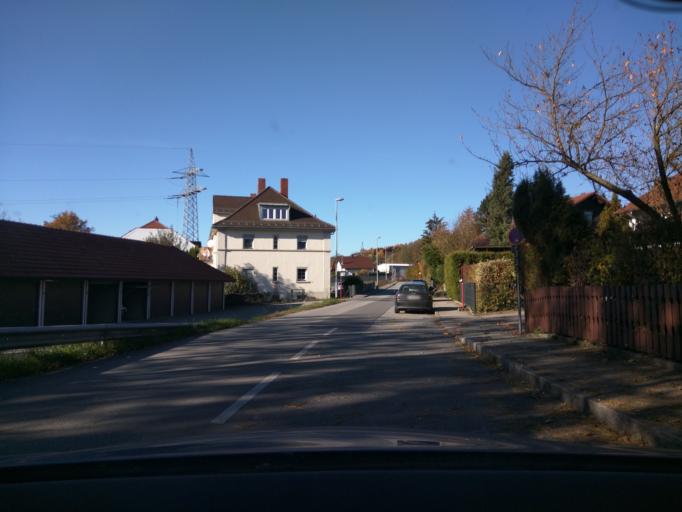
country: DE
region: Bavaria
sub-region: Lower Bavaria
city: Passau
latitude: 48.5786
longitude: 13.4133
